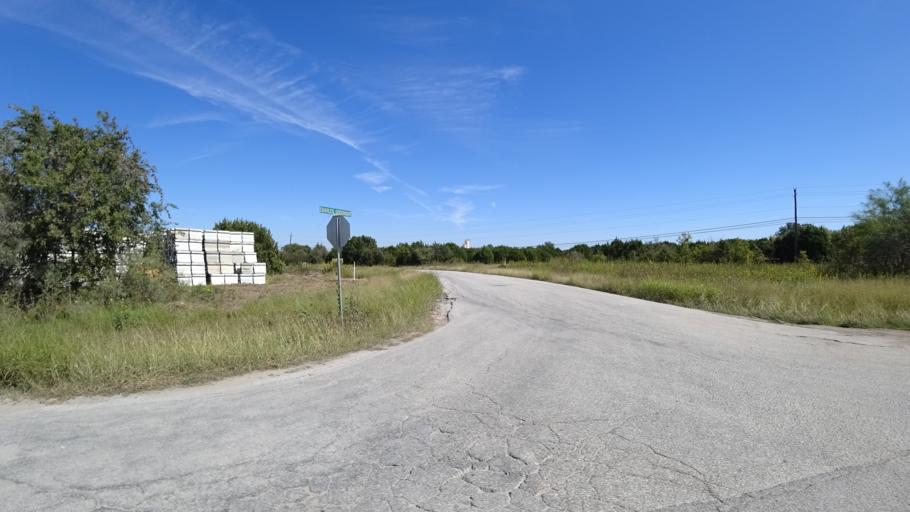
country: US
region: Texas
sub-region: Travis County
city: Austin
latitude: 30.1886
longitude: -97.7030
